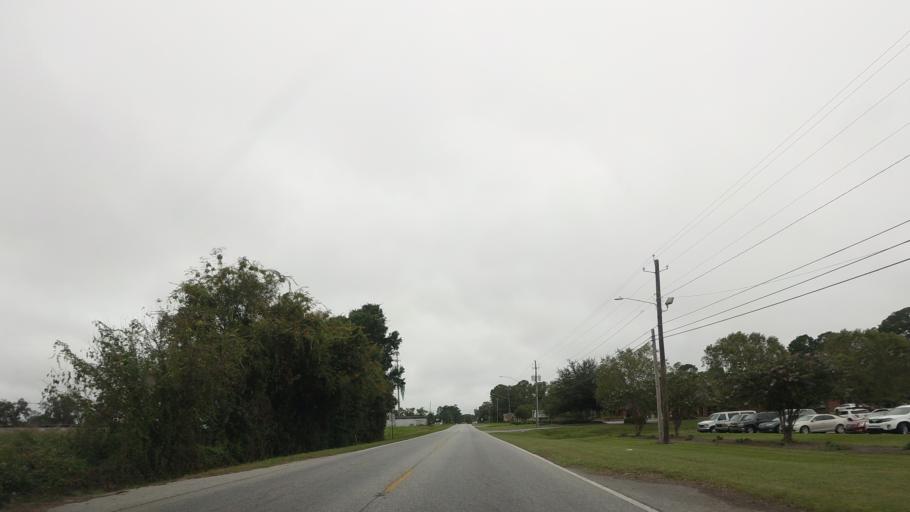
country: US
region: Georgia
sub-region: Lowndes County
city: Valdosta
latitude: 30.8186
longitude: -83.2645
